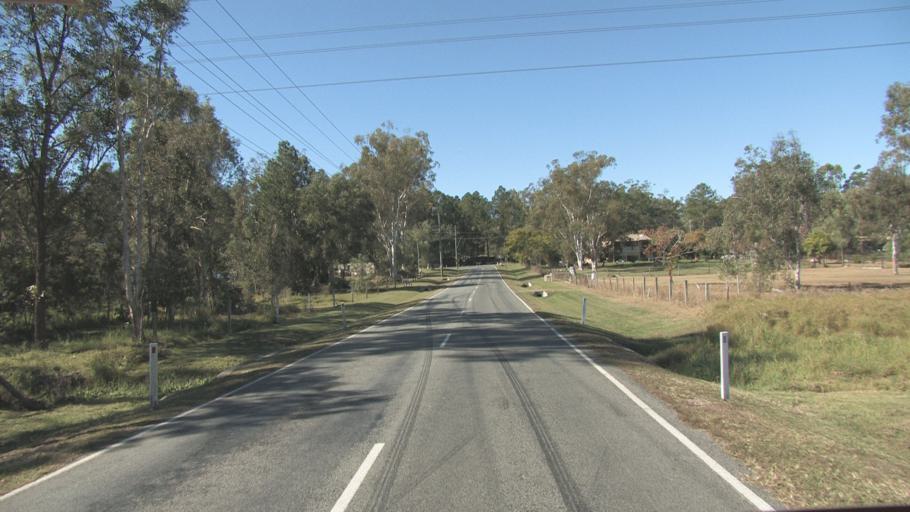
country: AU
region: Queensland
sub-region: Logan
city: Logan Reserve
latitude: -27.7196
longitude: 153.0628
